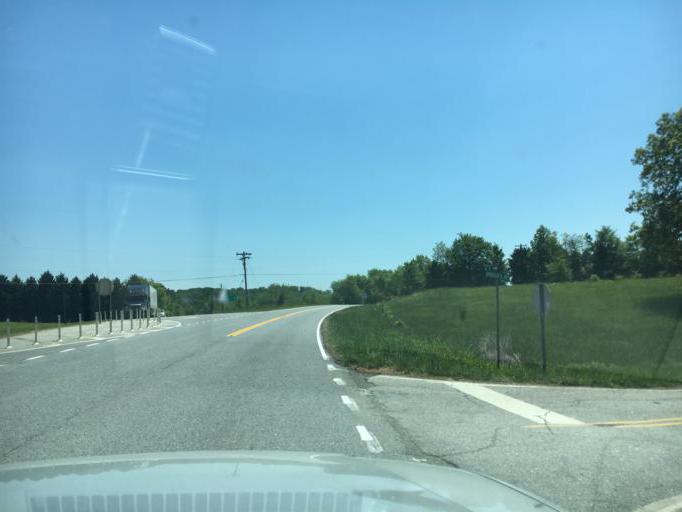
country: US
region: South Carolina
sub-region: Cherokee County
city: Blacksburg
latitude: 35.1512
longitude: -81.5734
